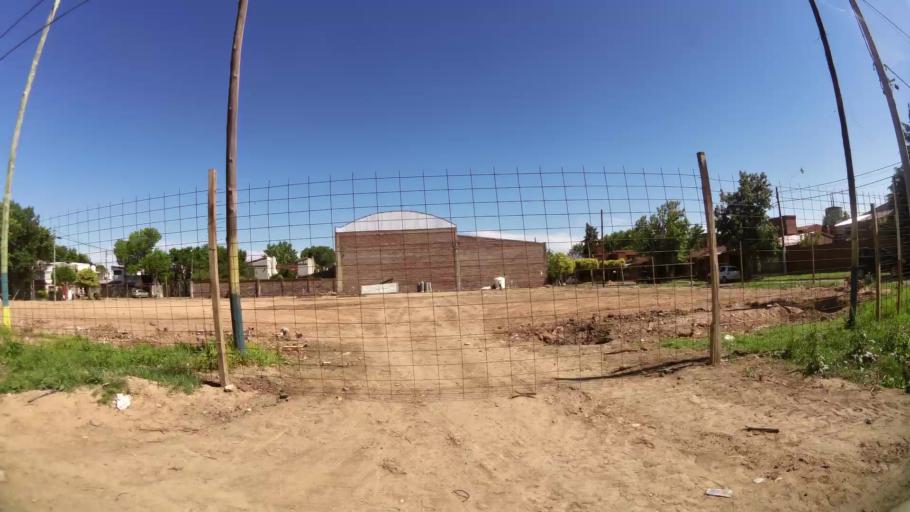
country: AR
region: Santa Fe
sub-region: Departamento de Rosario
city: Rosario
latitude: -32.9330
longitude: -60.6980
